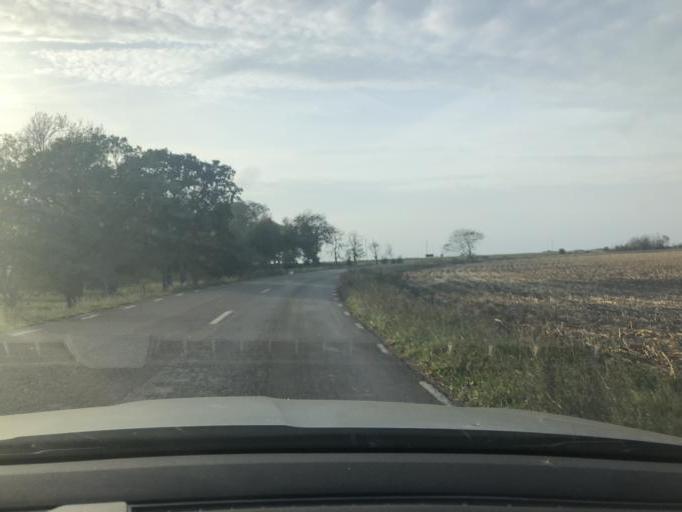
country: SE
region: Kalmar
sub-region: Morbylanga Kommun
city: Moerbylanga
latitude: 56.2346
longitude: 16.4141
